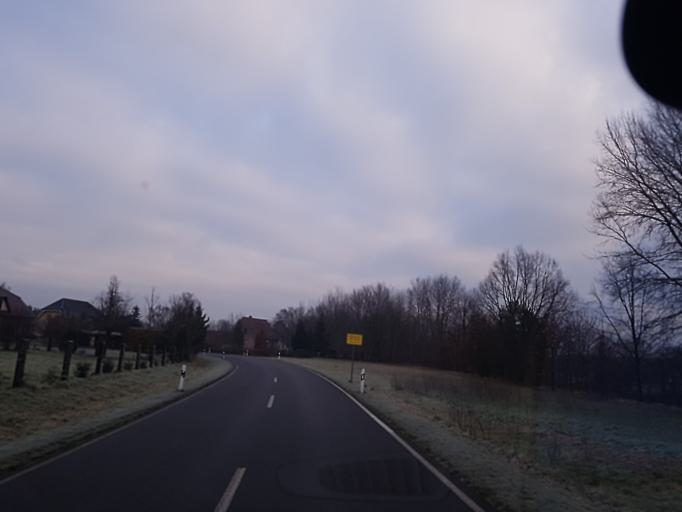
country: DE
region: Brandenburg
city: Finsterwalde
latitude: 51.6853
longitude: 13.7256
